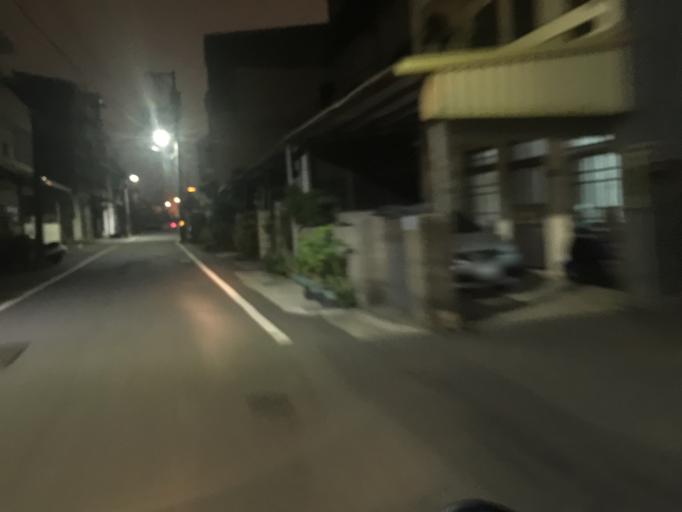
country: TW
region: Taiwan
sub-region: Miaoli
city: Miaoli
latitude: 24.5784
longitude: 120.8284
